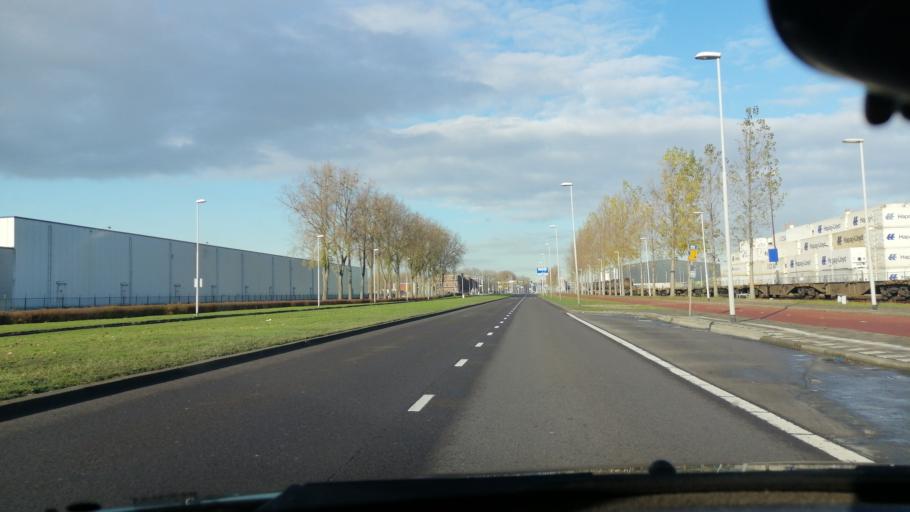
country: NL
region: South Holland
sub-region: Gemeente Albrandswaard
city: Rhoon
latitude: 51.8808
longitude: 4.4310
